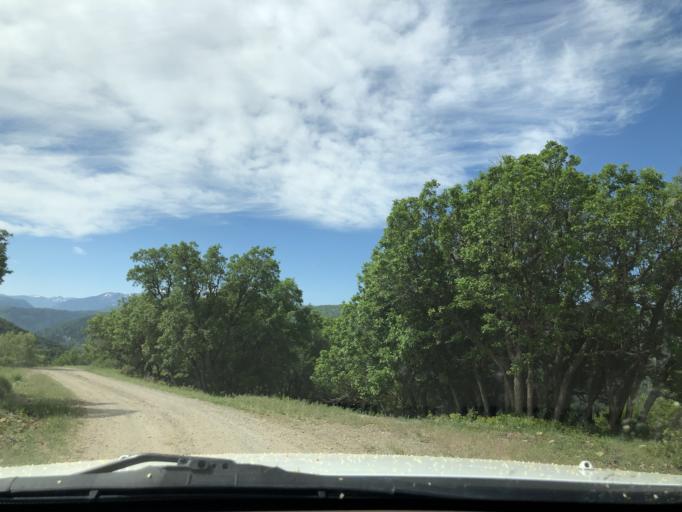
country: US
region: Colorado
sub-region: Delta County
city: Paonia
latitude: 39.0014
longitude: -107.3463
